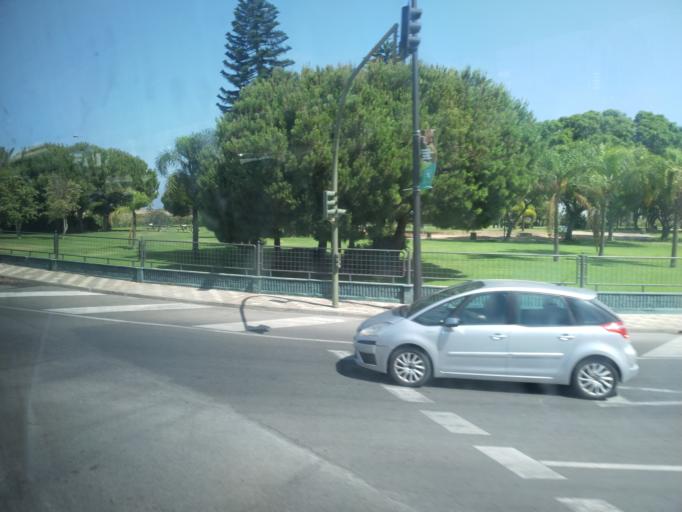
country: ES
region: Andalusia
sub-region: Provincia de Cadiz
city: San Fernando
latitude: 36.4564
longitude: -6.2146
